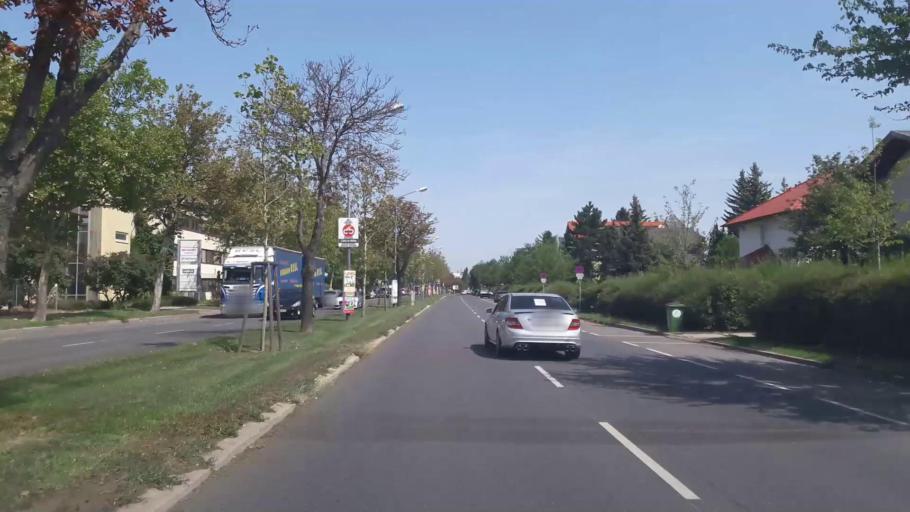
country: AT
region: Lower Austria
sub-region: Politischer Bezirk Modling
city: Vosendorf
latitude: 48.1412
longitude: 16.3595
